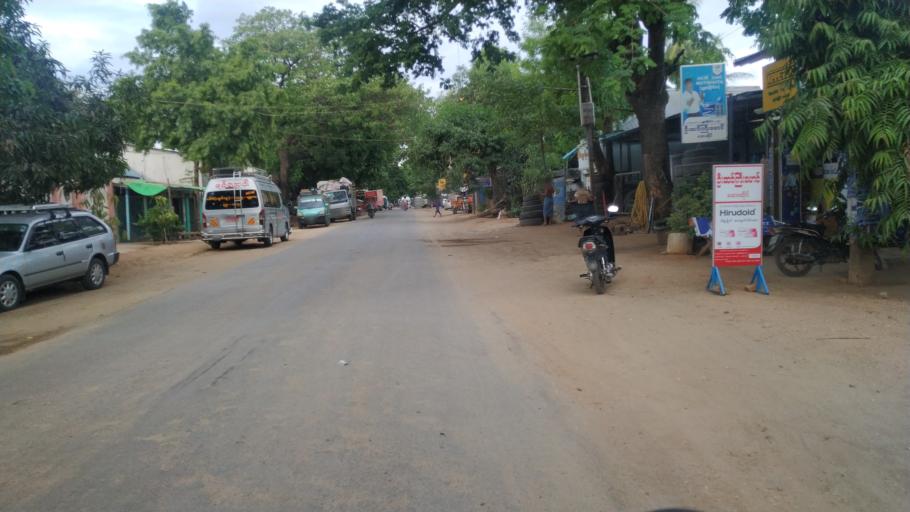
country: MM
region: Magway
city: Pakokku
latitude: 21.3357
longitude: 95.0755
